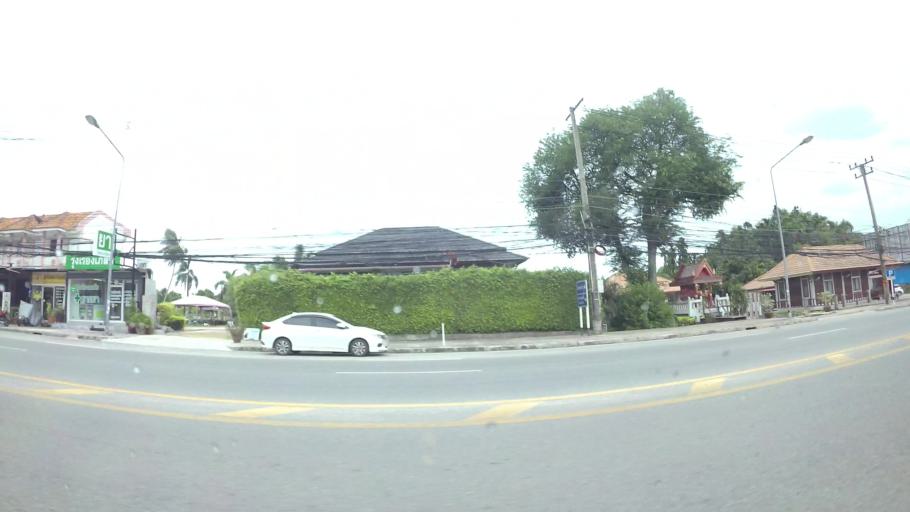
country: TH
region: Chon Buri
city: Si Racha
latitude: 13.1566
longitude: 100.9710
